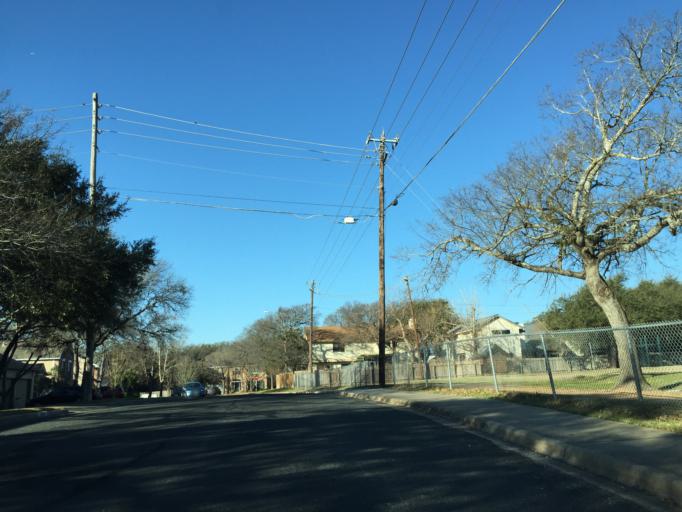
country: US
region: Texas
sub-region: Williamson County
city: Jollyville
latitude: 30.4451
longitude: -97.7633
